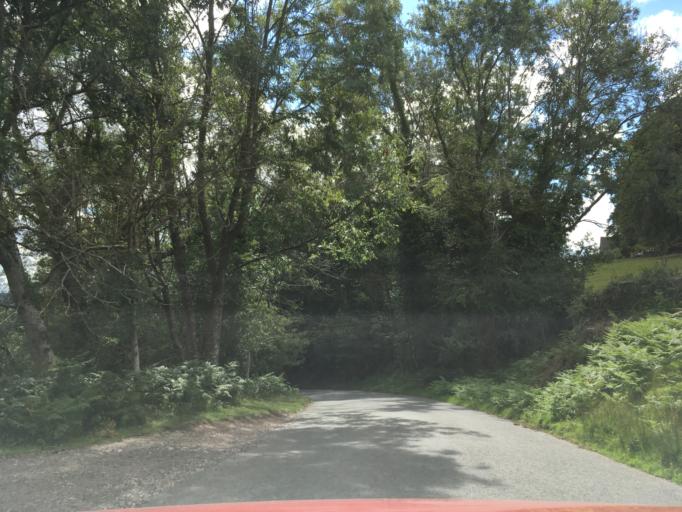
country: GB
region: England
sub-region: Gloucestershire
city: Bream
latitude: 51.7478
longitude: -2.5664
